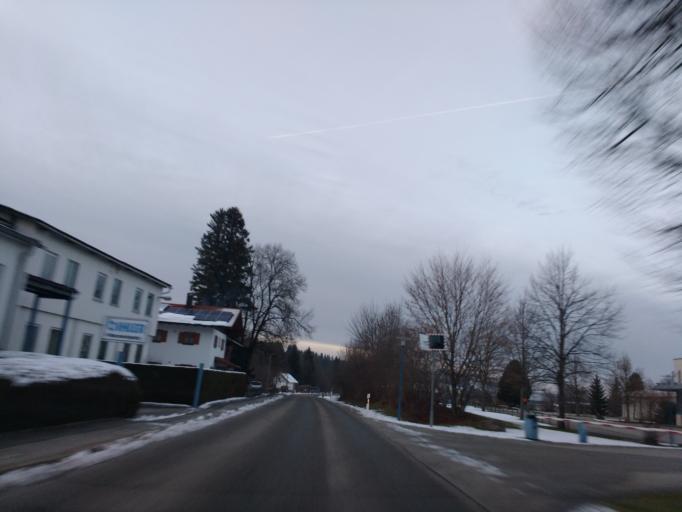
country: DE
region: Bavaria
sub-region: Swabia
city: Halblech
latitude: 47.6347
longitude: 10.8194
